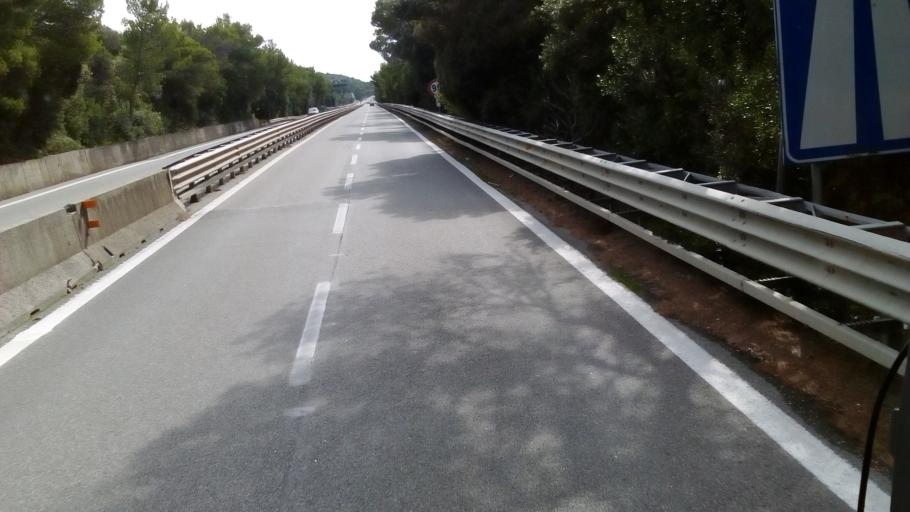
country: IT
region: Tuscany
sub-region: Provincia di Livorno
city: Quercianella
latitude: 43.4445
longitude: 10.3838
